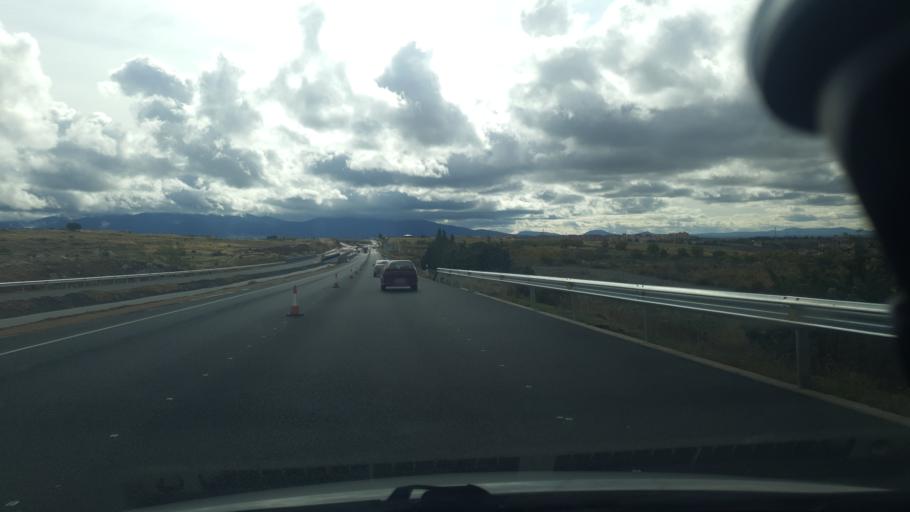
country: ES
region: Castille and Leon
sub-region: Provincia de Segovia
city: San Cristobal de Segovia
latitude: 40.9636
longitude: -4.0873
